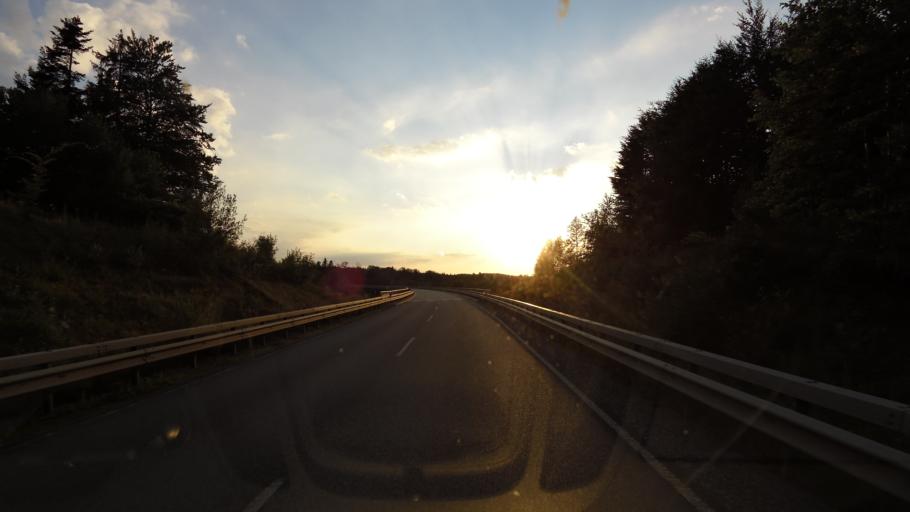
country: DE
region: Bavaria
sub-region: Upper Bavaria
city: Traunstein
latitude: 47.8939
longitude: 12.6367
